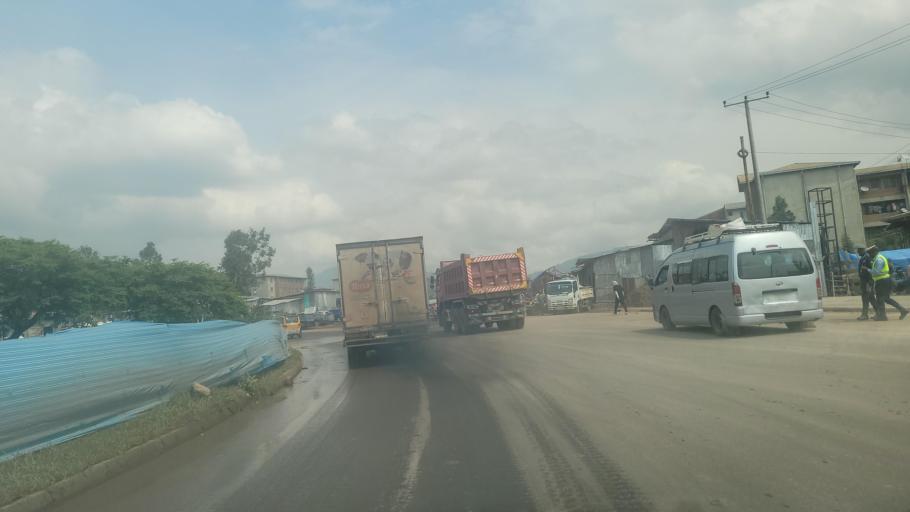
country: ET
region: Adis Abeba
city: Addis Ababa
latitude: 8.9550
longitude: 38.6972
